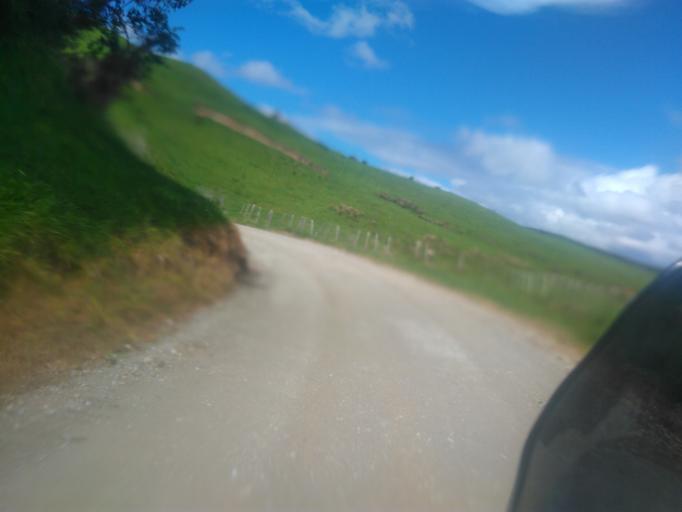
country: NZ
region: Hawke's Bay
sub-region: Wairoa District
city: Wairoa
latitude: -38.7764
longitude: 177.6330
